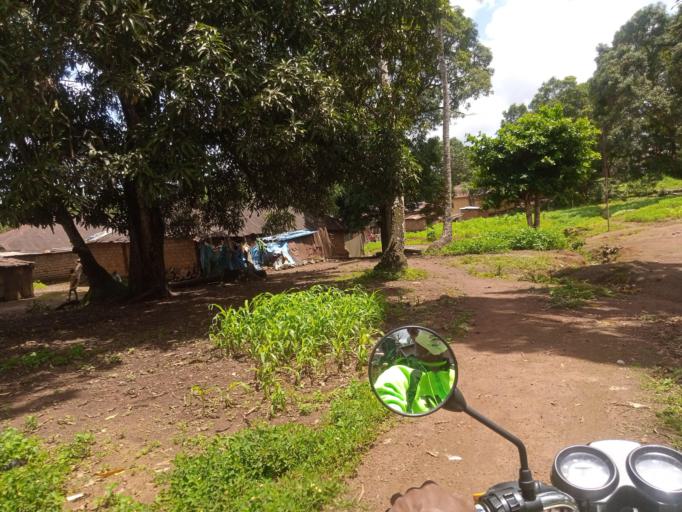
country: SL
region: Northern Province
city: Port Loko
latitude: 8.7621
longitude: -12.7899
